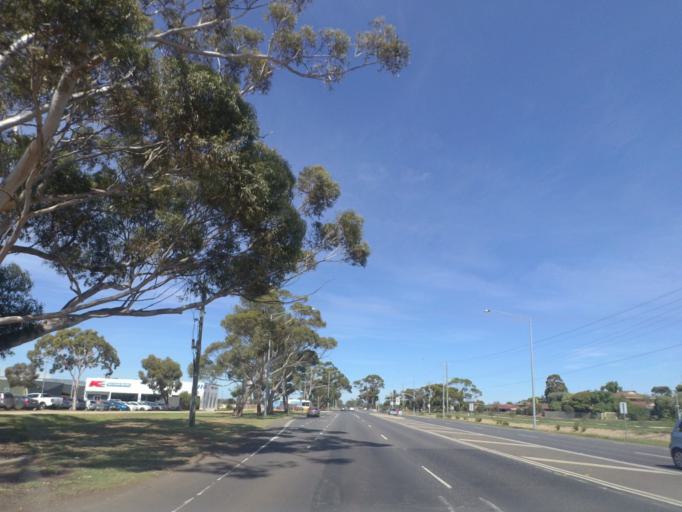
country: AU
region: Victoria
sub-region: Melton
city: Melton West
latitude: -37.6846
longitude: 144.5646
